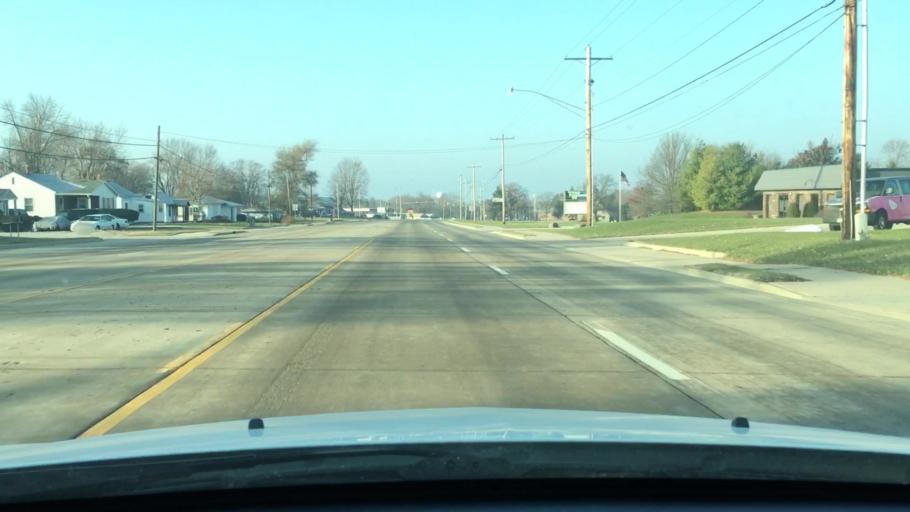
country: US
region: Illinois
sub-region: Tazewell County
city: Washington
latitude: 40.6965
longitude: -89.4705
